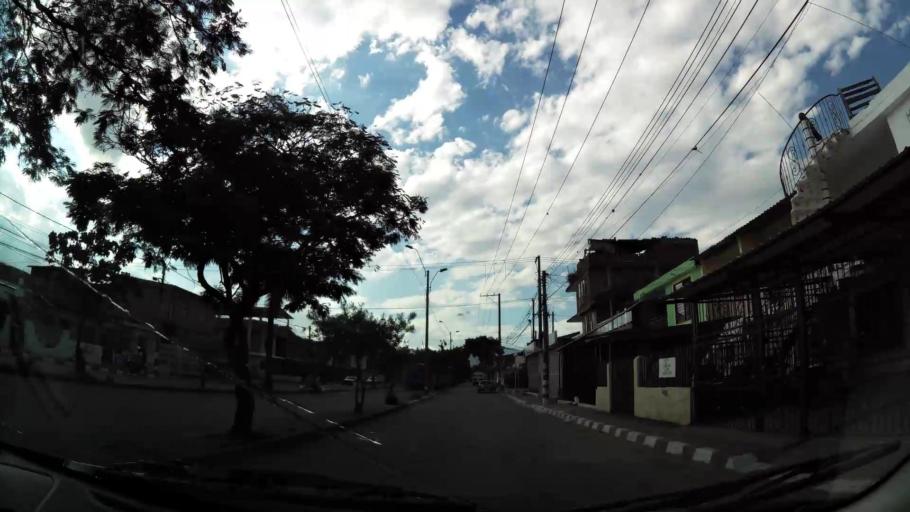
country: CO
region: Valle del Cauca
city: Cali
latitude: 3.4137
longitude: -76.4920
